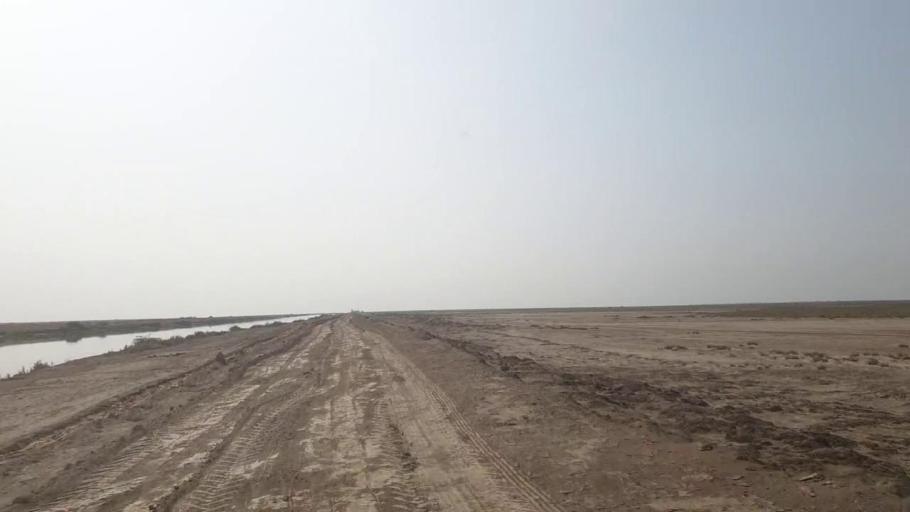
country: PK
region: Sindh
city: Kadhan
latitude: 24.3337
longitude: 68.8394
